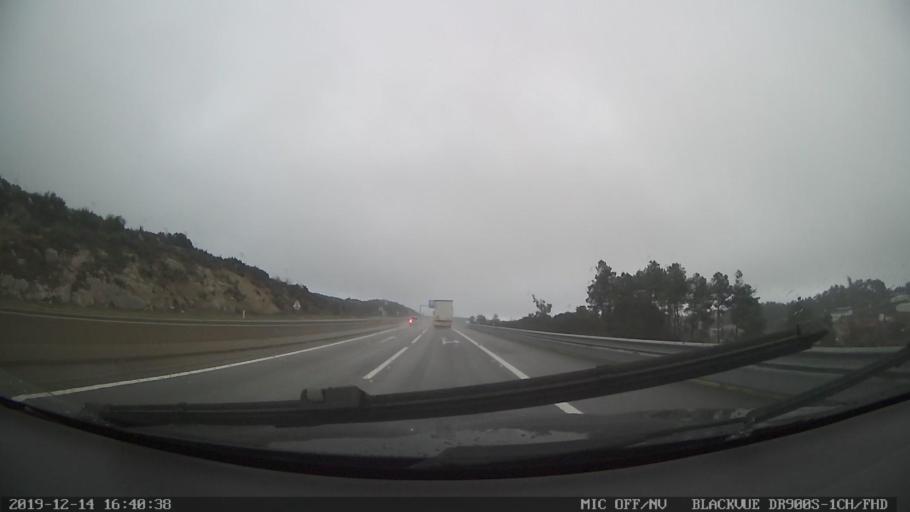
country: PT
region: Vila Real
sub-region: Murca
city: Murca
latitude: 41.3791
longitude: -7.5199
